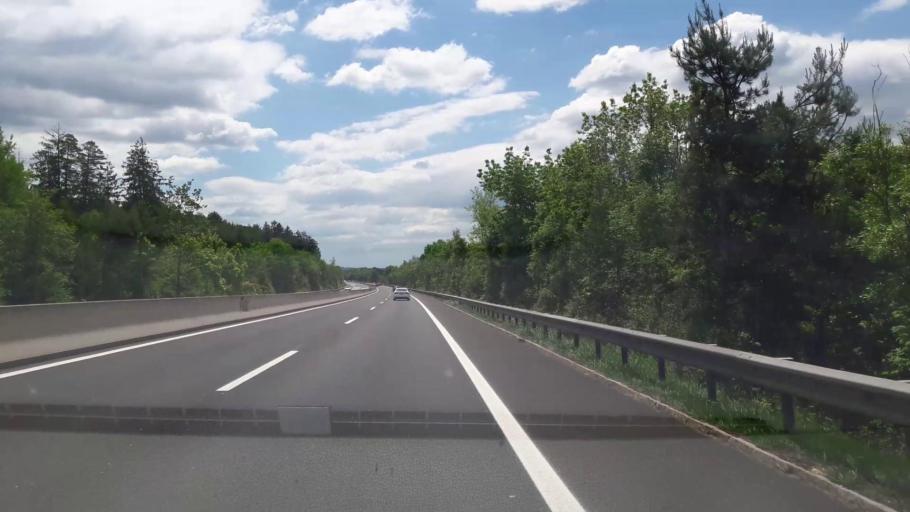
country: AT
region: Burgenland
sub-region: Politischer Bezirk Oberwart
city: Markt Allhau
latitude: 47.3175
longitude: 16.0619
